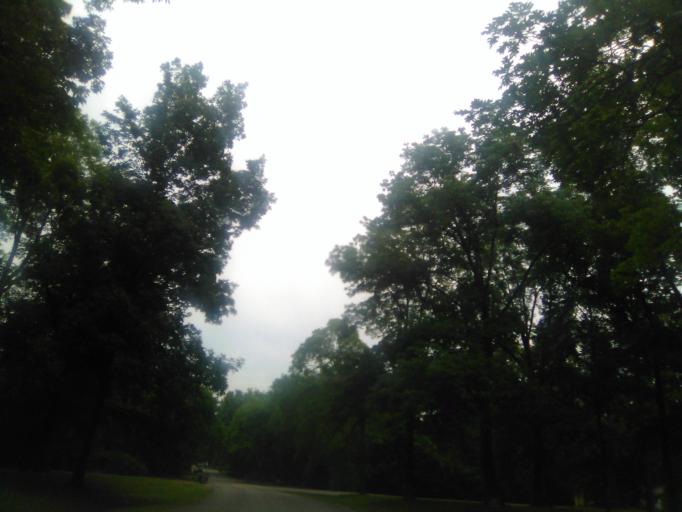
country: US
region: Tennessee
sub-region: Davidson County
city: Belle Meade
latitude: 36.1118
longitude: -86.8811
